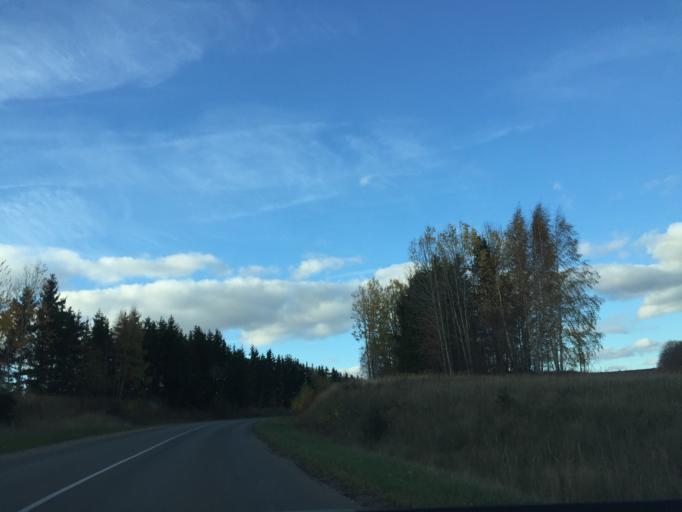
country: LV
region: Tukuma Rajons
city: Tukums
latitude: 56.9938
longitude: 23.0889
